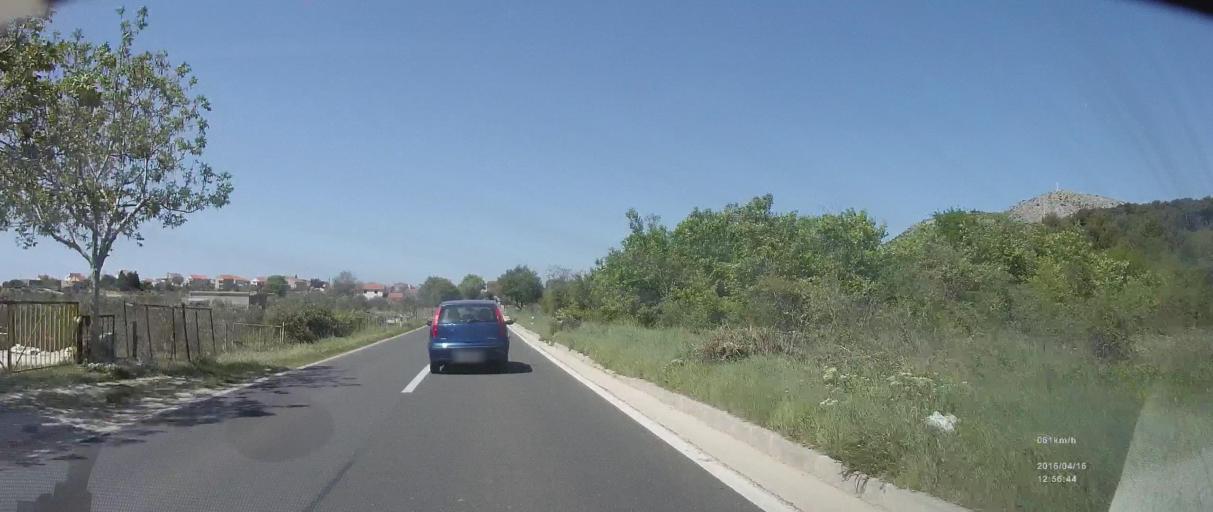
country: HR
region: Sibensko-Kniniska
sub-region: Grad Sibenik
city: Brodarica
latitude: 43.7021
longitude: 15.9383
